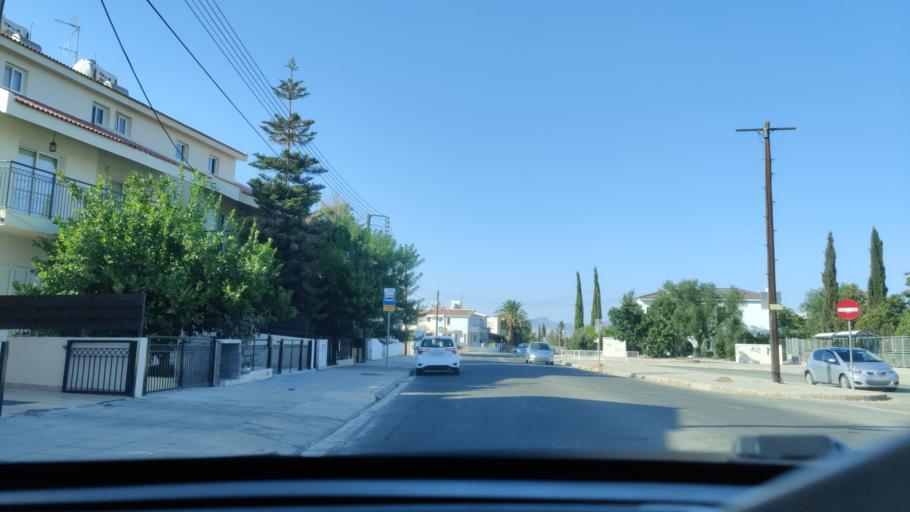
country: CY
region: Lefkosia
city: Tseri
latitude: 35.1187
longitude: 33.3263
